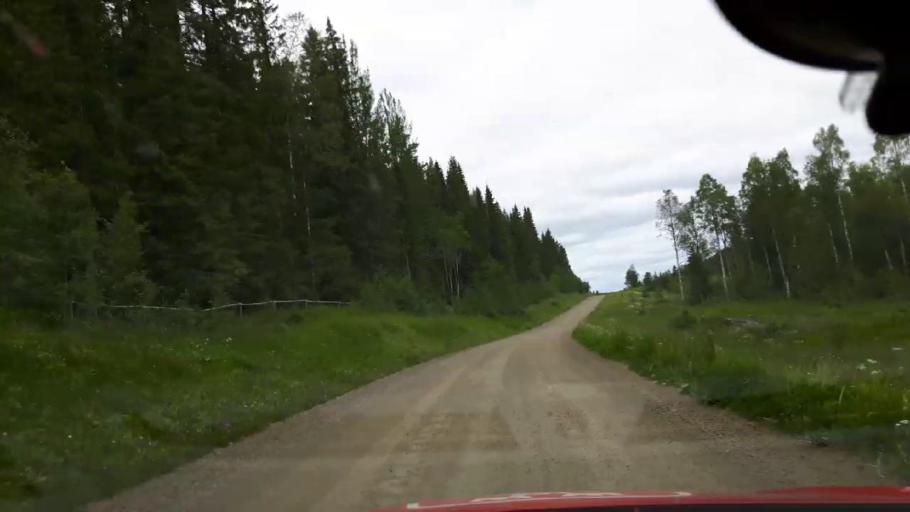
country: SE
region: Jaemtland
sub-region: OEstersunds Kommun
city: Brunflo
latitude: 62.9278
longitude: 15.0016
